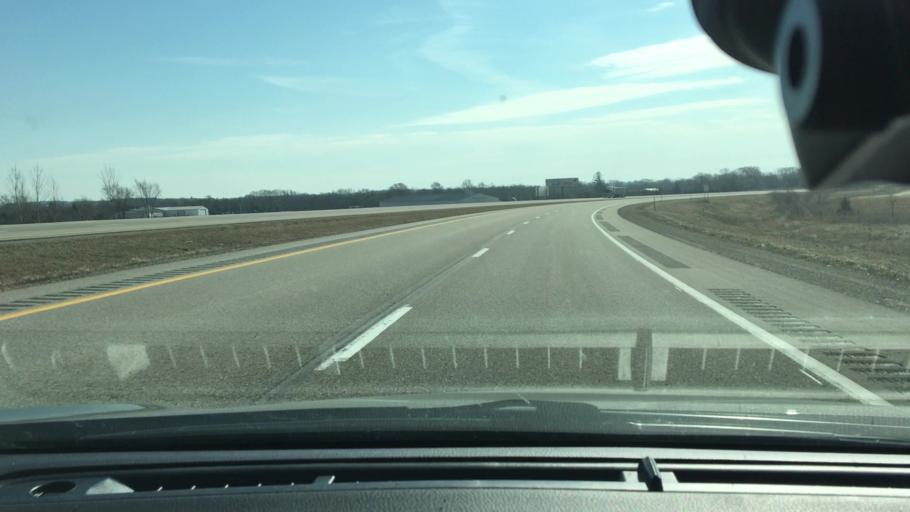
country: US
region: Iowa
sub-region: Floyd County
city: Charles City
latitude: 43.0387
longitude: -92.6611
